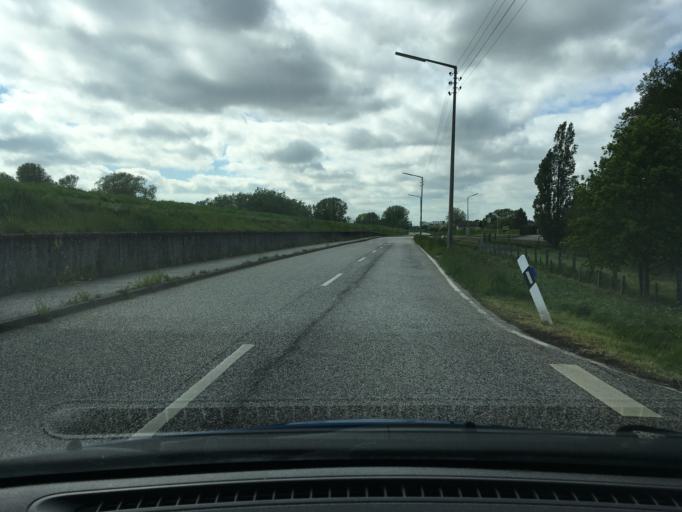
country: DE
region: Hamburg
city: Rothenburgsort
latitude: 53.4729
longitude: 10.0457
